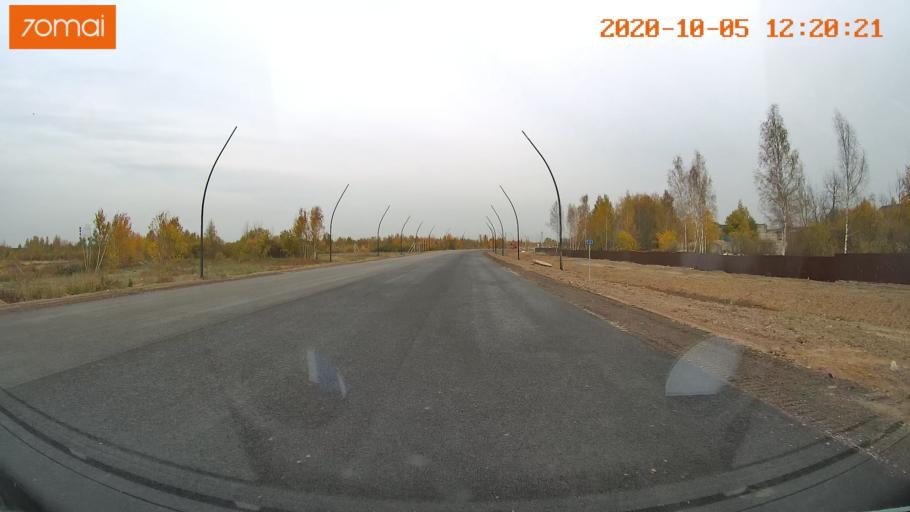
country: RU
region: Ivanovo
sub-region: Gorod Ivanovo
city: Ivanovo
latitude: 56.9625
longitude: 40.9307
